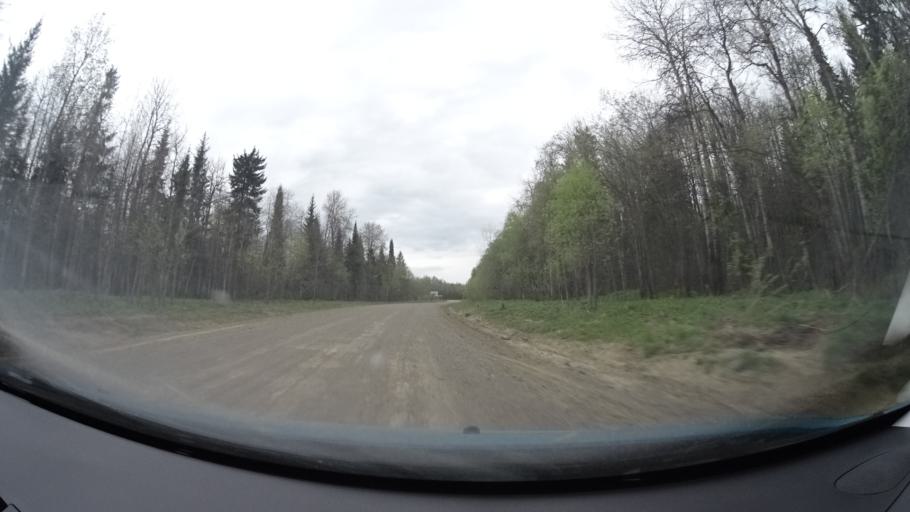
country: RU
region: Perm
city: Kuyeda
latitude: 56.5911
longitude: 55.7039
